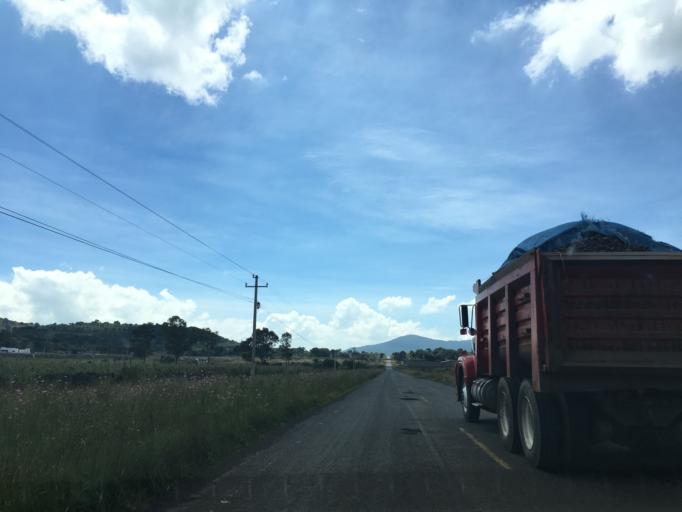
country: MX
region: Michoacan
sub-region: Morelia
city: Cuto de la Esperanza
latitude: 19.7153
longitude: -101.3411
